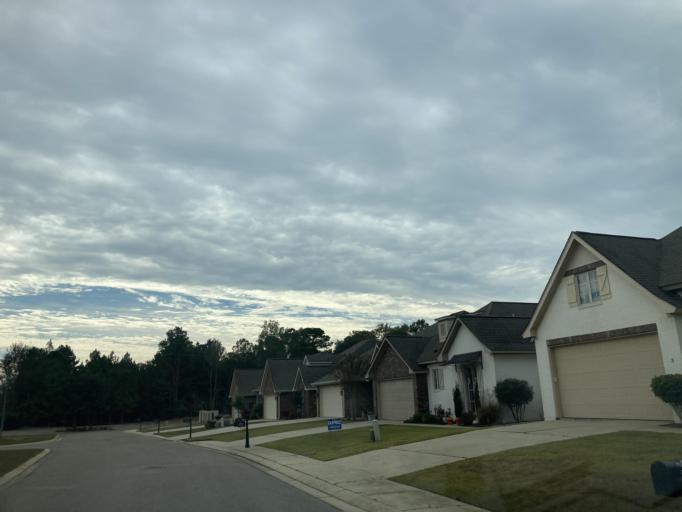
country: US
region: Mississippi
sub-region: Lamar County
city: West Hattiesburg
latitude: 31.3225
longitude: -89.3972
